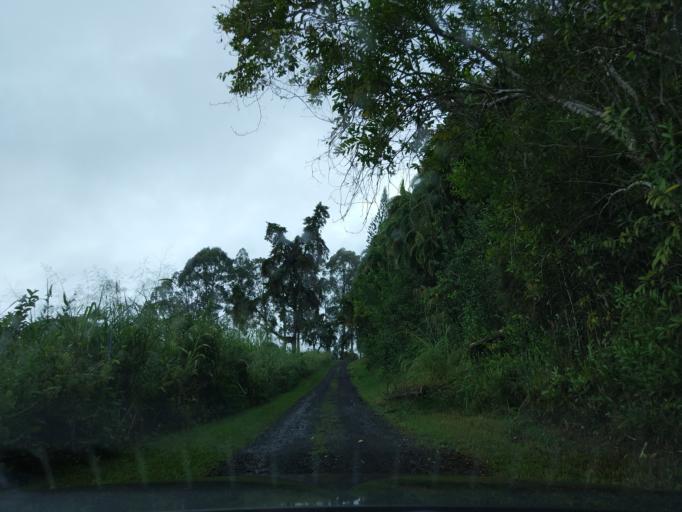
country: US
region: Hawaii
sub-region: Hawaii County
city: Pepeekeo
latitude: 19.8753
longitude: -155.1405
